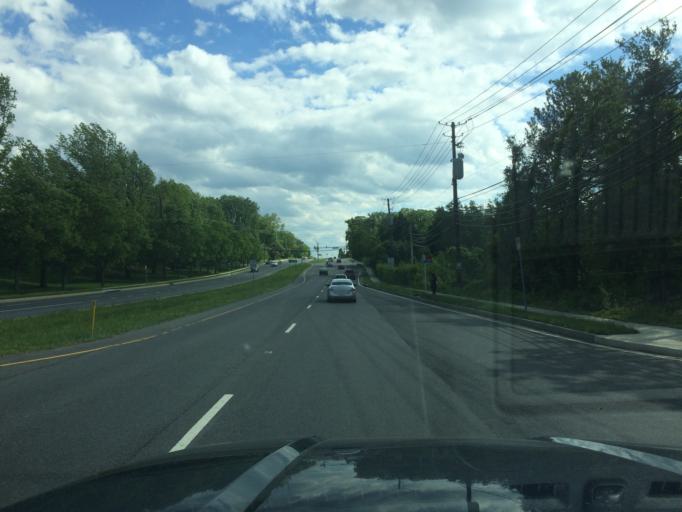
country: US
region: Maryland
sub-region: Montgomery County
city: Olney
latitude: 39.1391
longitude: -77.0685
